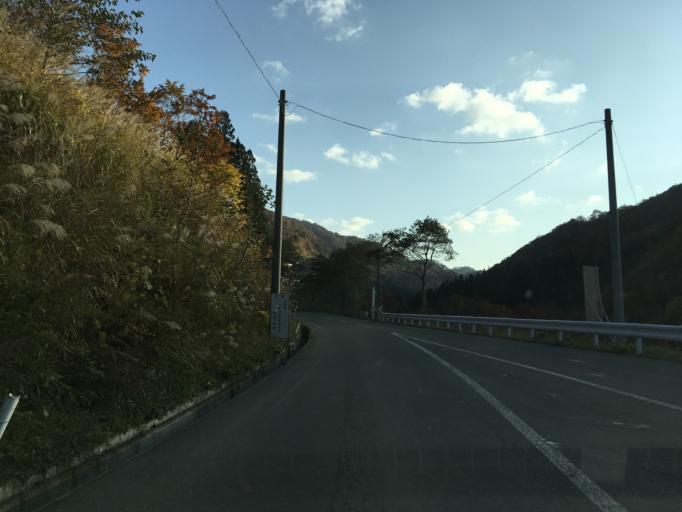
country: JP
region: Akita
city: Yuzawa
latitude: 39.0303
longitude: 140.7277
